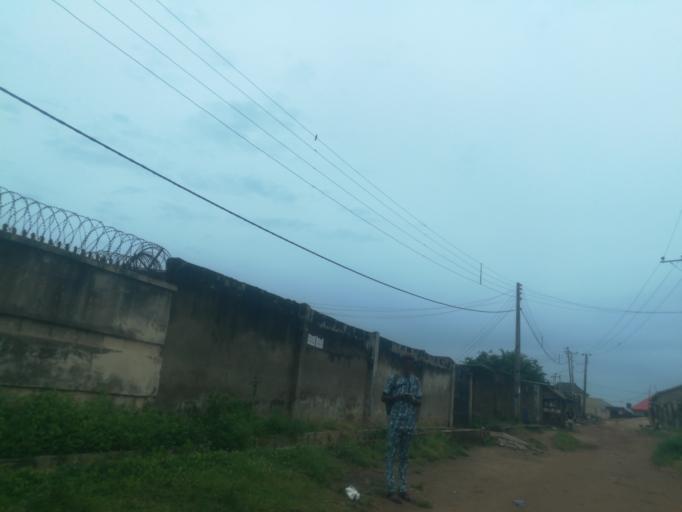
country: NG
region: Oyo
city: Egbeda
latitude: 7.3872
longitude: 3.9852
